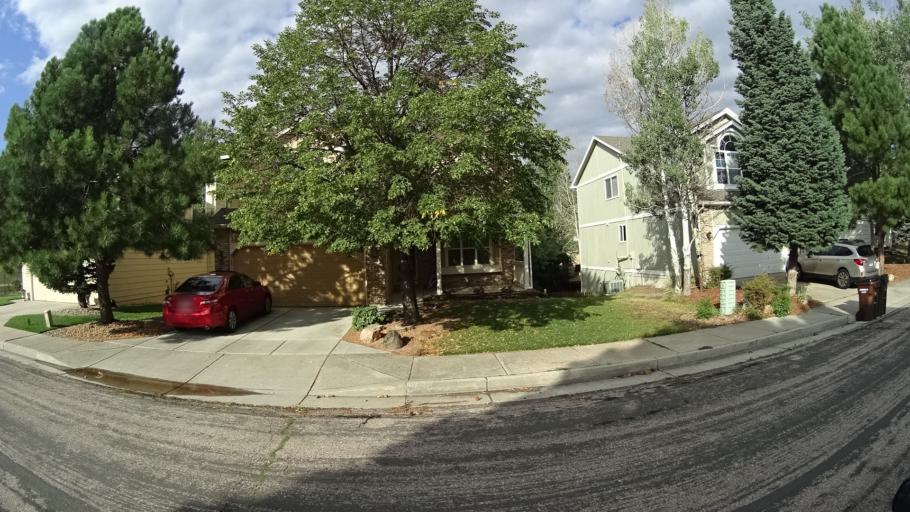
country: US
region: Colorado
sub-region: El Paso County
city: Manitou Springs
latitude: 38.9095
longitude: -104.8571
